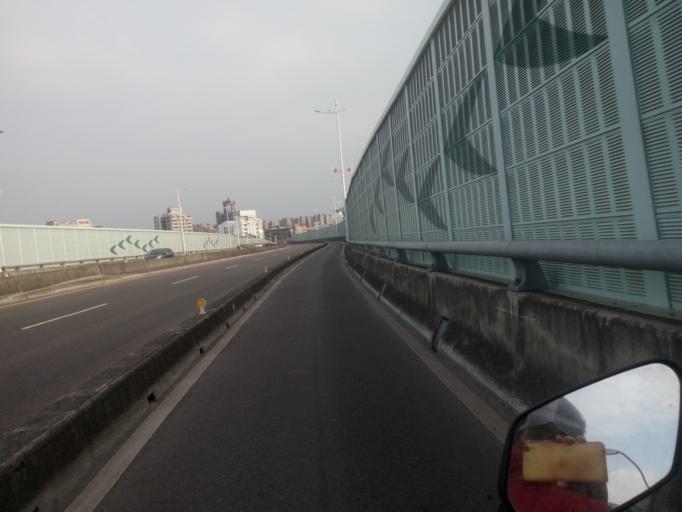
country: TW
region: Taiwan
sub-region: Chiayi
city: Jiayi Shi
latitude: 23.4754
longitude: 120.4336
